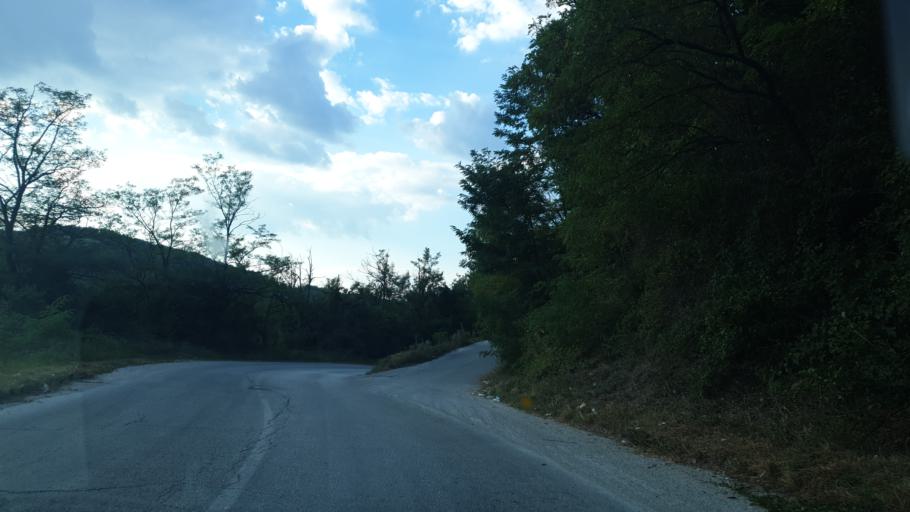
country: RS
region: Central Serbia
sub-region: Zlatiborski Okrug
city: Uzice
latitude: 43.8625
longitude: 19.9081
